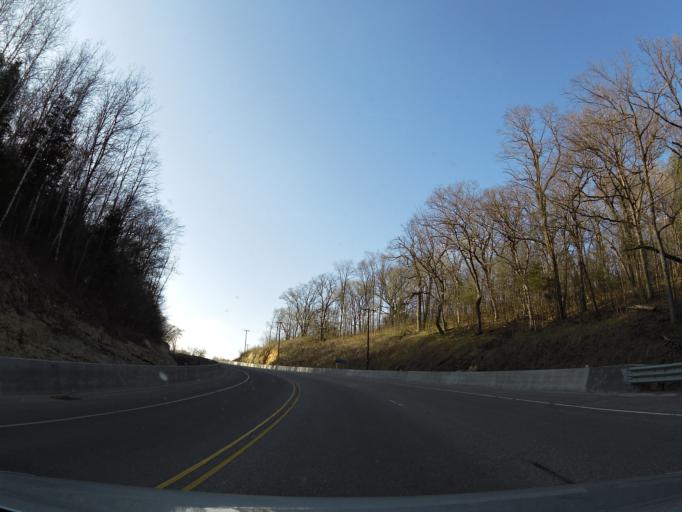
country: US
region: Minnesota
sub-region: Washington County
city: Afton
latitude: 44.8340
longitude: -92.7290
